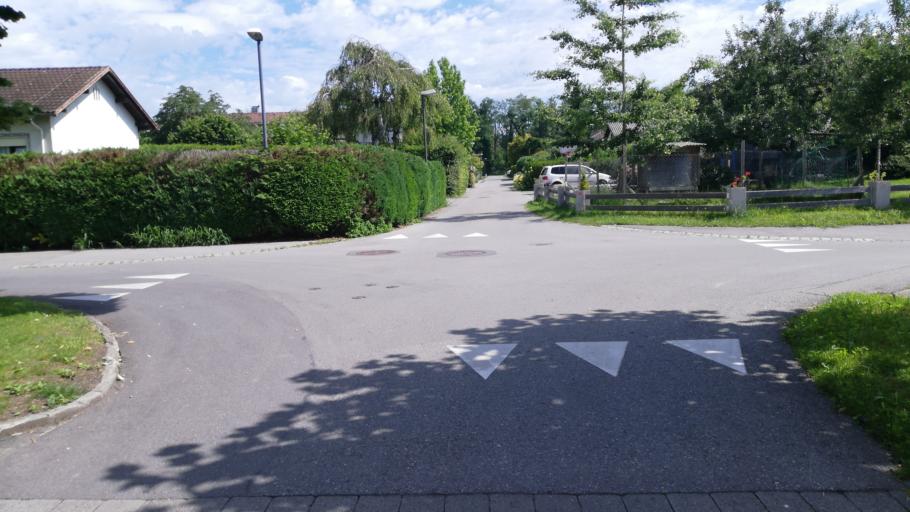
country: AT
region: Vorarlberg
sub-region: Politischer Bezirk Feldkirch
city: Nofels
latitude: 47.2601
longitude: 9.5658
